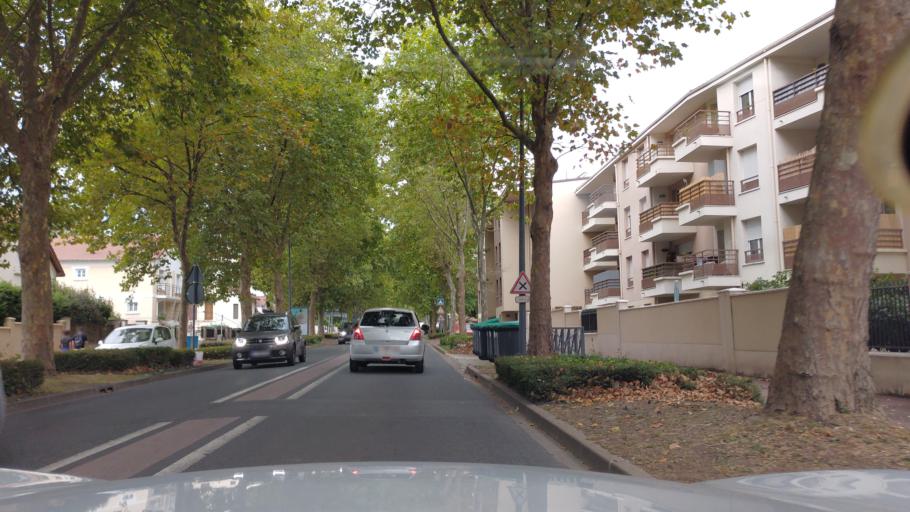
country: FR
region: Ile-de-France
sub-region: Departement de Seine-et-Marne
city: Brie-Comte-Robert
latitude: 48.6983
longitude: 2.6049
